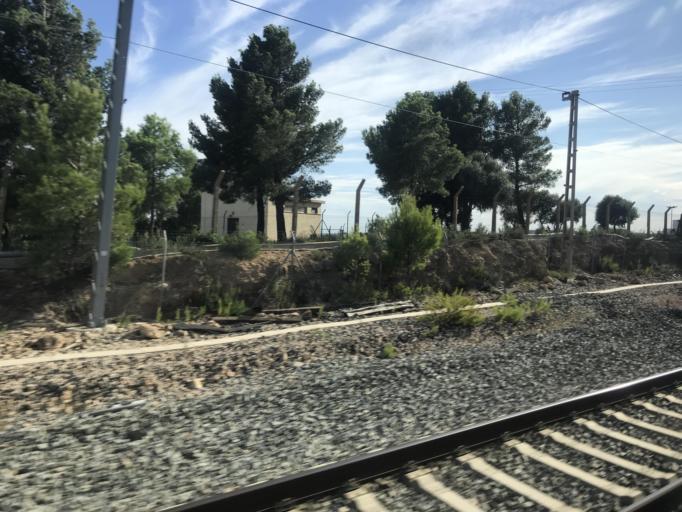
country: ES
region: Catalonia
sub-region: Provincia de Tarragona
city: l'Ametlla de Mar
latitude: 40.9552
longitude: 0.8705
